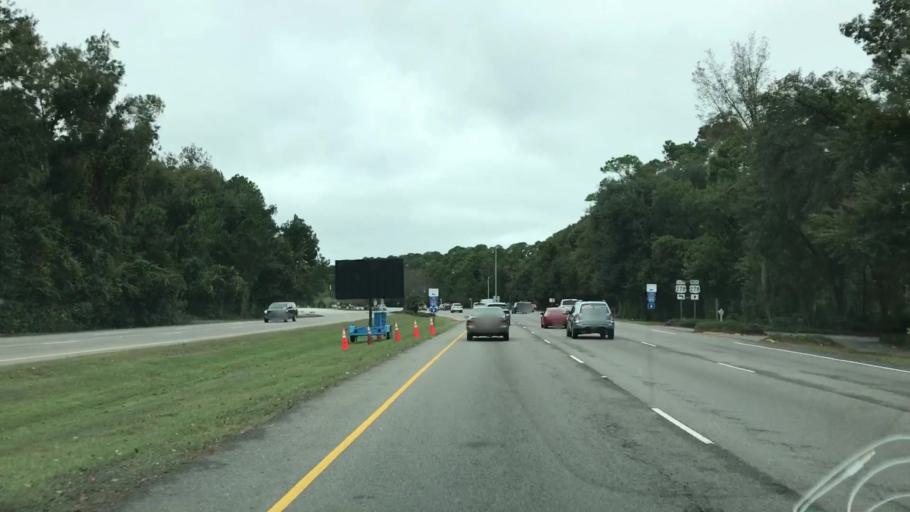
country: US
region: South Carolina
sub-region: Beaufort County
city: Hilton Head Island
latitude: 32.2155
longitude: -80.7354
